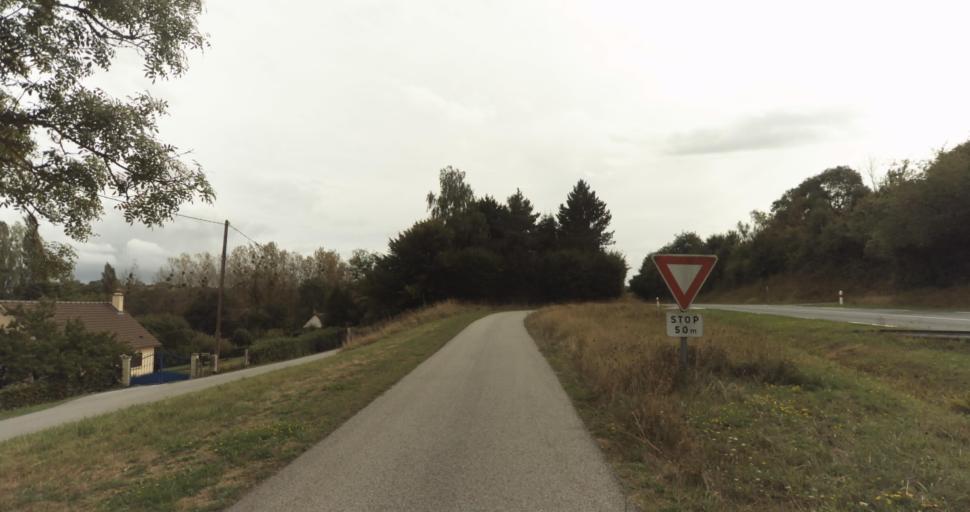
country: FR
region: Lower Normandy
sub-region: Departement de l'Orne
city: Gace
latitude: 48.8160
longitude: 0.2804
